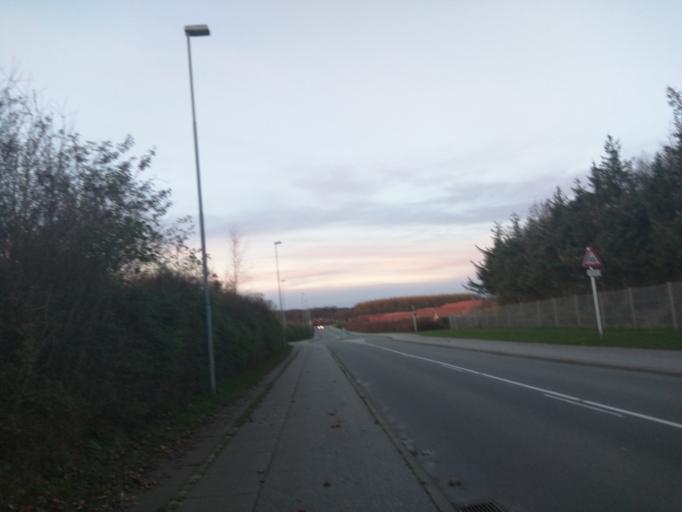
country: DK
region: Central Jutland
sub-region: Skanderborg Kommune
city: Horning
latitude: 56.0898
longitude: 10.0284
